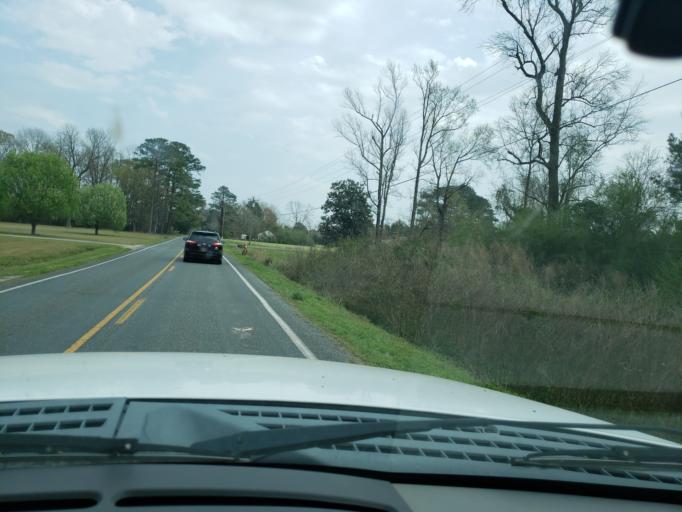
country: US
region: North Carolina
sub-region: Duplin County
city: Beulaville
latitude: 34.7763
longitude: -77.8214
